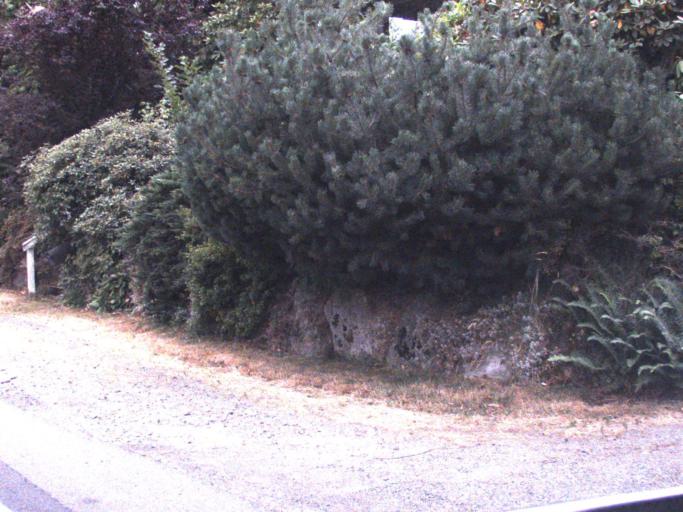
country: US
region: Washington
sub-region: King County
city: Carnation
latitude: 47.6296
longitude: -121.9119
